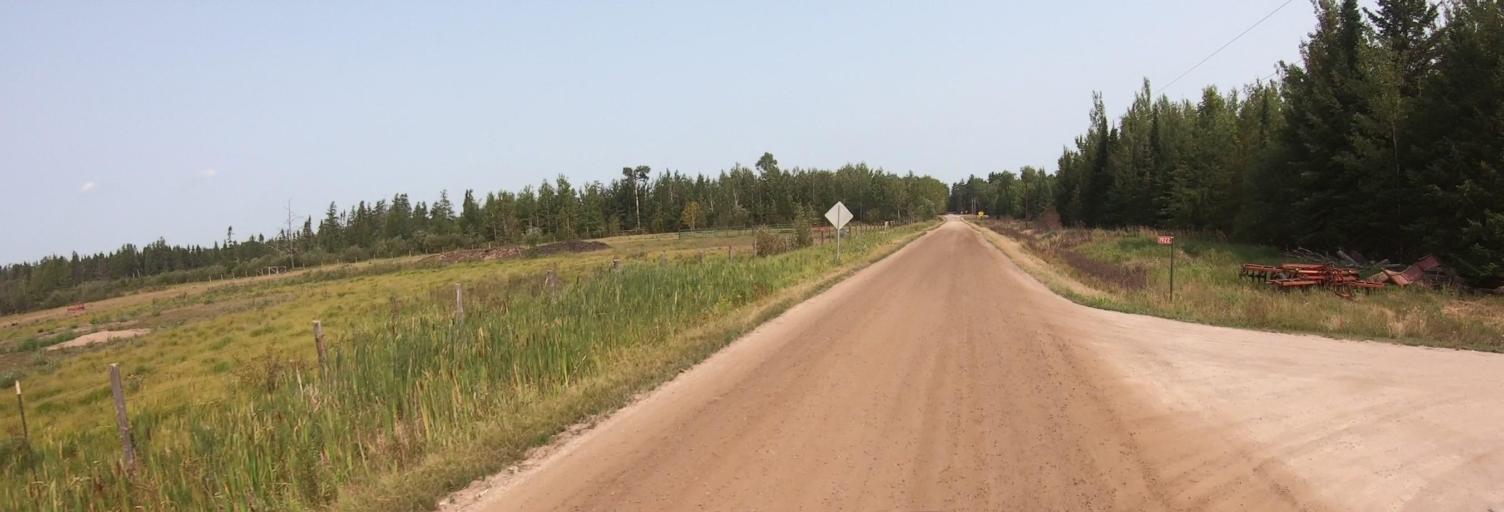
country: US
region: Minnesota
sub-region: Saint Louis County
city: Mountain Iron
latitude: 47.8638
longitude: -92.7400
